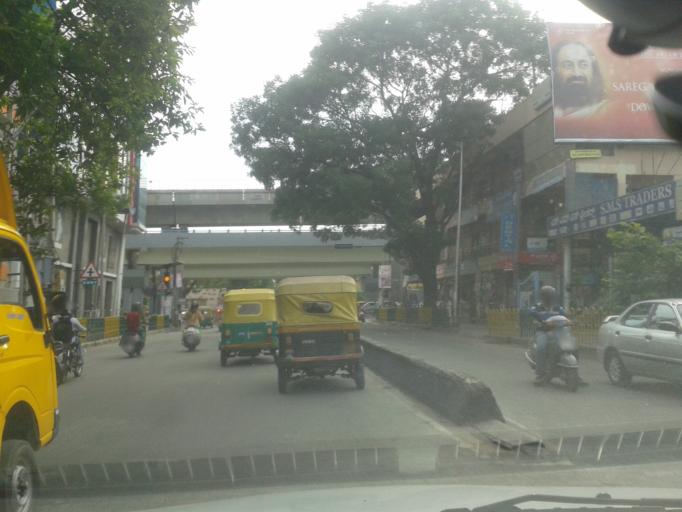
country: IN
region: Karnataka
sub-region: Bangalore Urban
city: Bangalore
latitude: 13.0040
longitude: 77.5499
